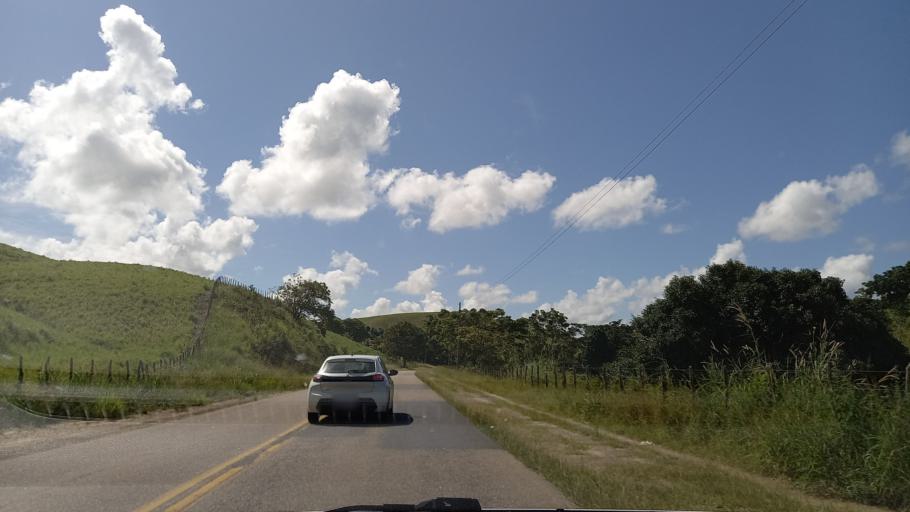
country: BR
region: Pernambuco
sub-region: Barreiros
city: Barreiros
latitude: -8.7537
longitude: -35.1713
